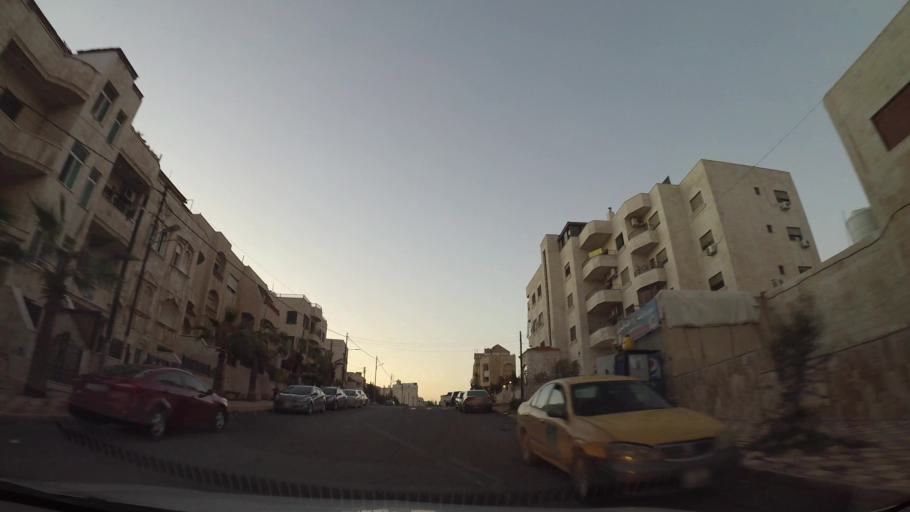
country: JO
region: Amman
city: Al Jubayhah
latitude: 31.9978
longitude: 35.8567
